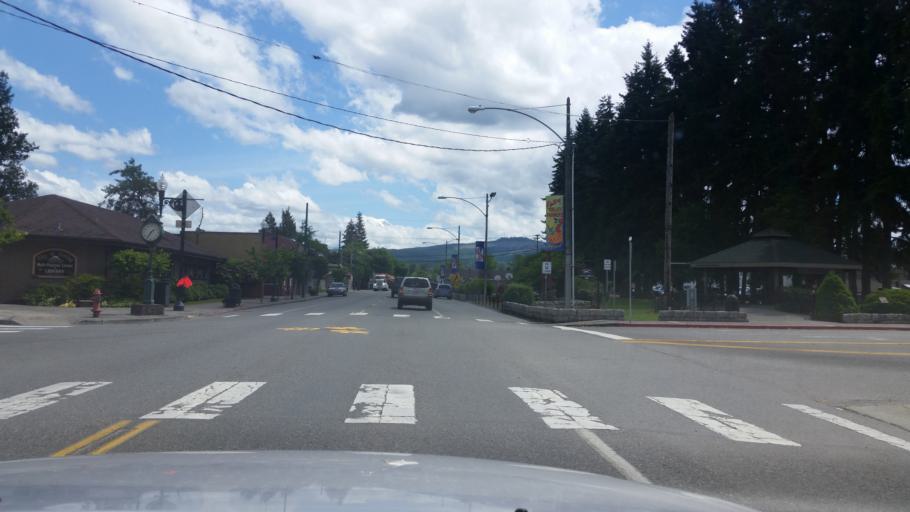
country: US
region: Washington
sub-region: Pierce County
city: Orting
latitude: 47.0971
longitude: -122.2032
